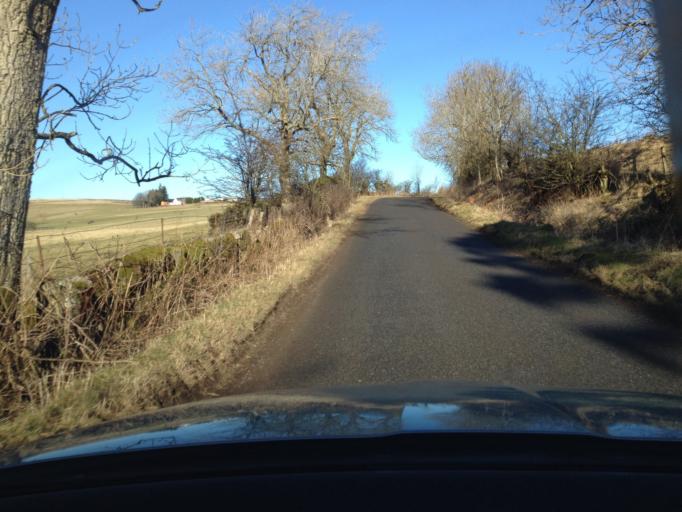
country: GB
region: Scotland
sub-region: Perth and Kinross
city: Bridge of Earn
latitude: 56.2936
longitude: -3.3970
